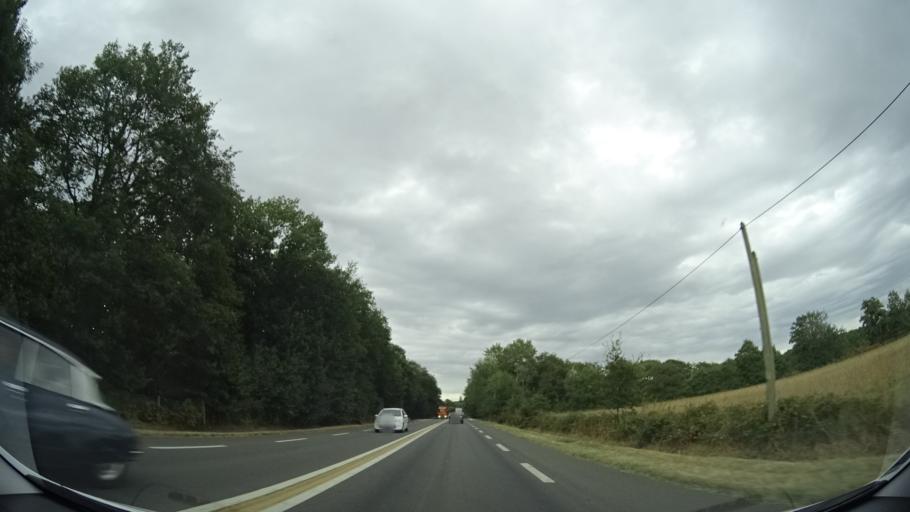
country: FR
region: Centre
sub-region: Departement du Loiret
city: Chateauneuf-sur-Loire
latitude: 47.8862
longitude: 2.2493
